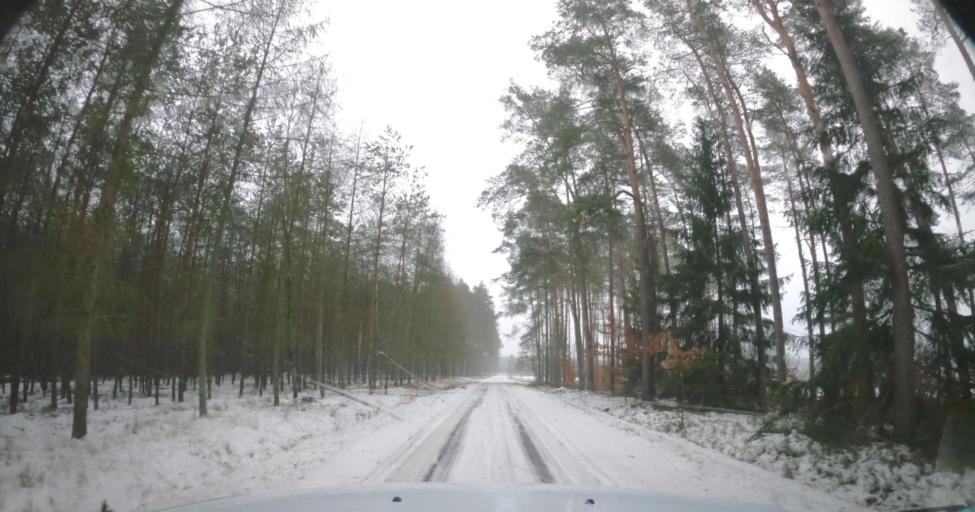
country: PL
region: West Pomeranian Voivodeship
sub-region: Powiat goleniowski
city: Goleniow
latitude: 53.6595
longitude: 14.8022
